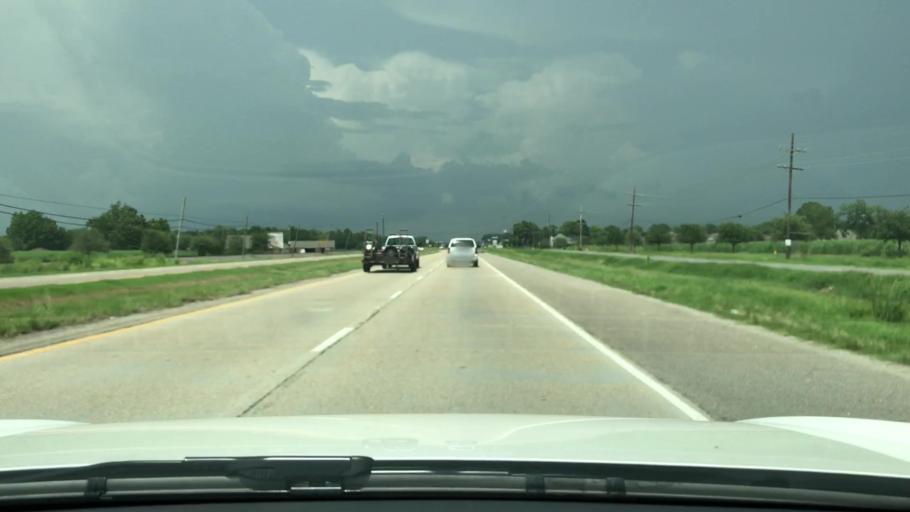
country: US
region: Louisiana
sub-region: West Baton Rouge Parish
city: Brusly
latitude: 30.3997
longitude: -91.2352
